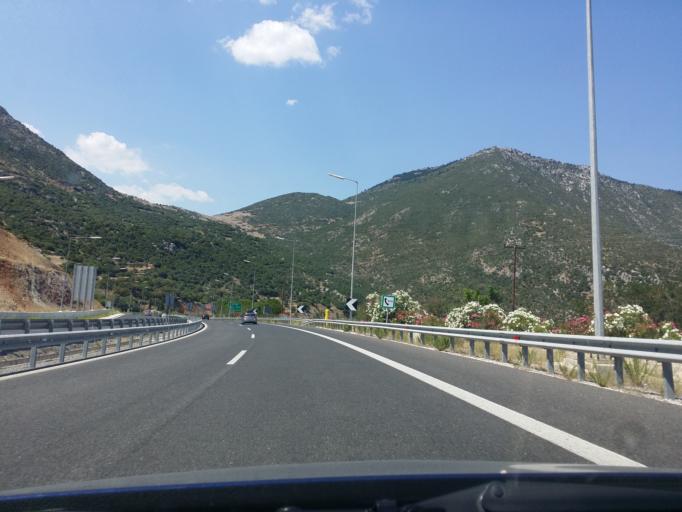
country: GR
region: Peloponnese
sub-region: Nomos Arkadias
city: Tripoli
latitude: 37.6766
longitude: 22.4891
